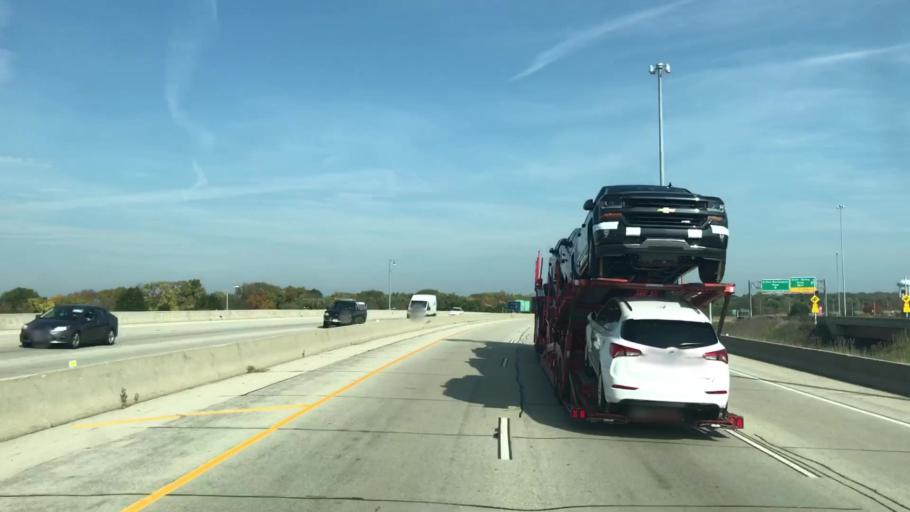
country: US
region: Wisconsin
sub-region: Milwaukee County
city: Whitefish Bay
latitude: 43.1163
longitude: -87.9186
